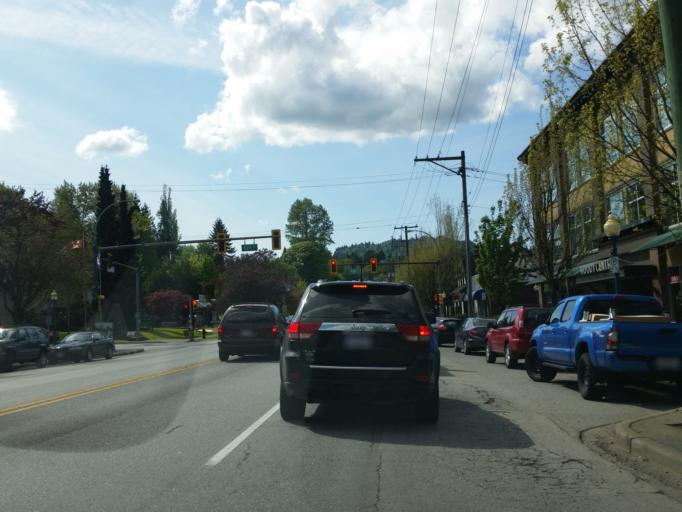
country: CA
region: British Columbia
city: Port Moody
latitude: 49.2768
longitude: -122.8558
